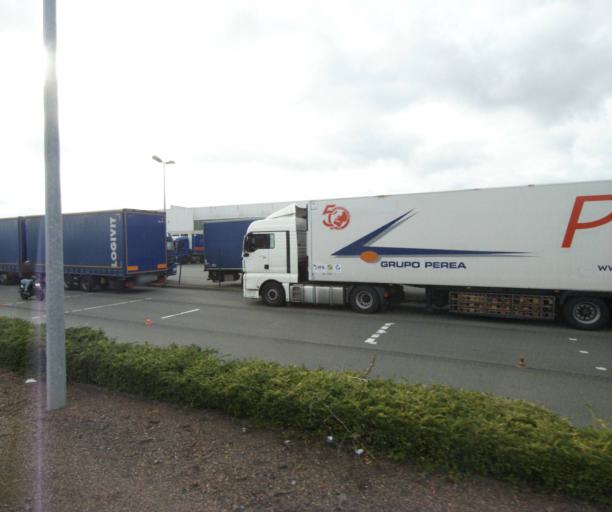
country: FR
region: Nord-Pas-de-Calais
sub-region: Departement du Nord
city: Bois-Grenier
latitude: 50.6542
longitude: 2.8951
